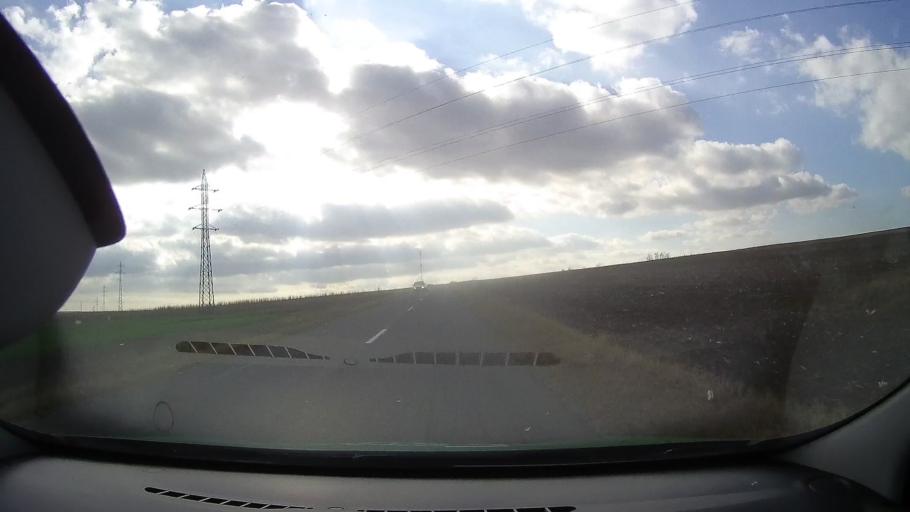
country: RO
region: Constanta
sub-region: Comuna Sacele
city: Sacele
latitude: 44.4951
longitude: 28.6567
